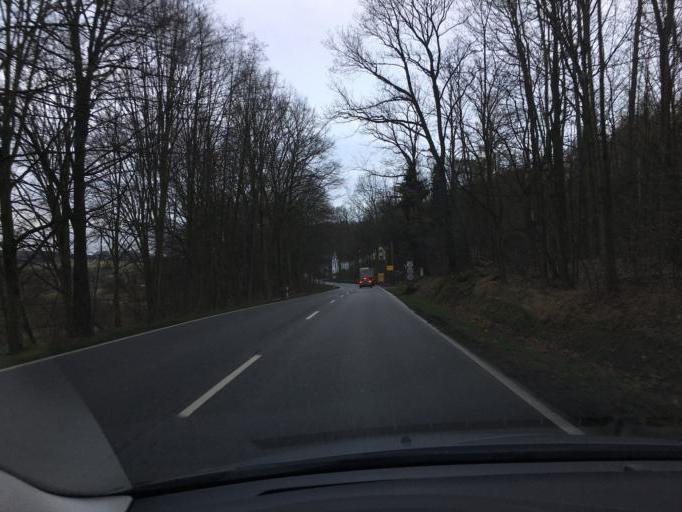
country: DE
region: Saxony
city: Waldenburg
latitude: 50.8819
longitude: 12.6209
